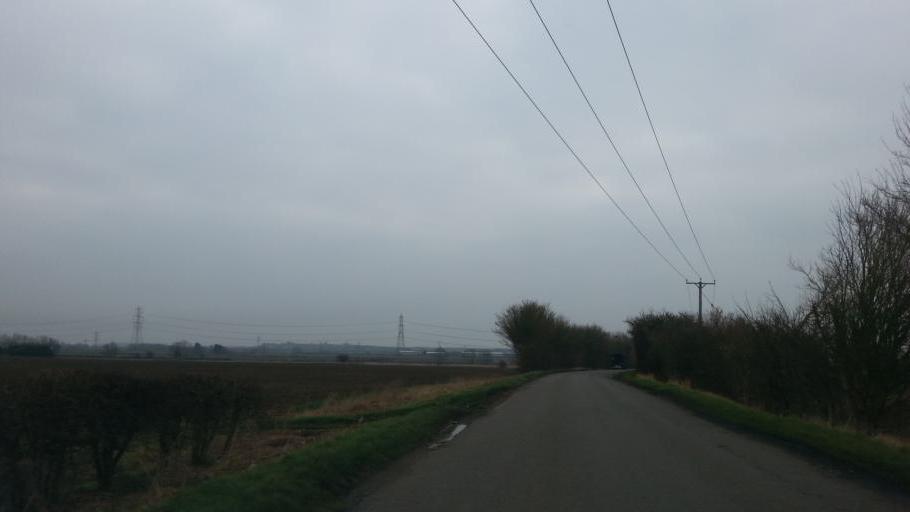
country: GB
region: England
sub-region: Lincolnshire
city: Long Bennington
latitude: 53.0022
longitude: -0.7818
